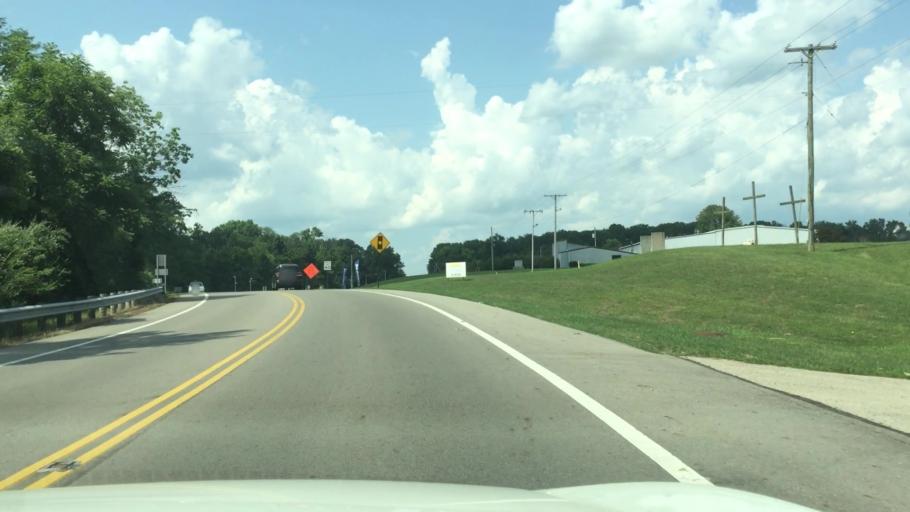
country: US
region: Ohio
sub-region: Clark County
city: Northridge
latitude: 39.9771
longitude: -83.7840
